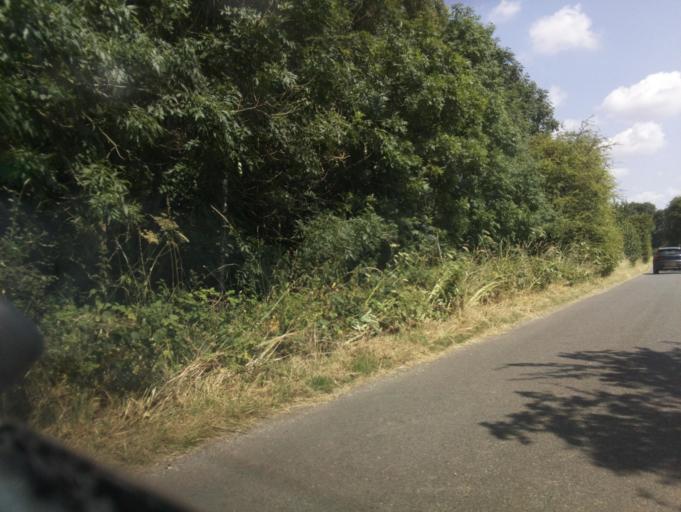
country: GB
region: England
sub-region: Gloucestershire
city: Donnington
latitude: 51.9479
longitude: -1.7274
